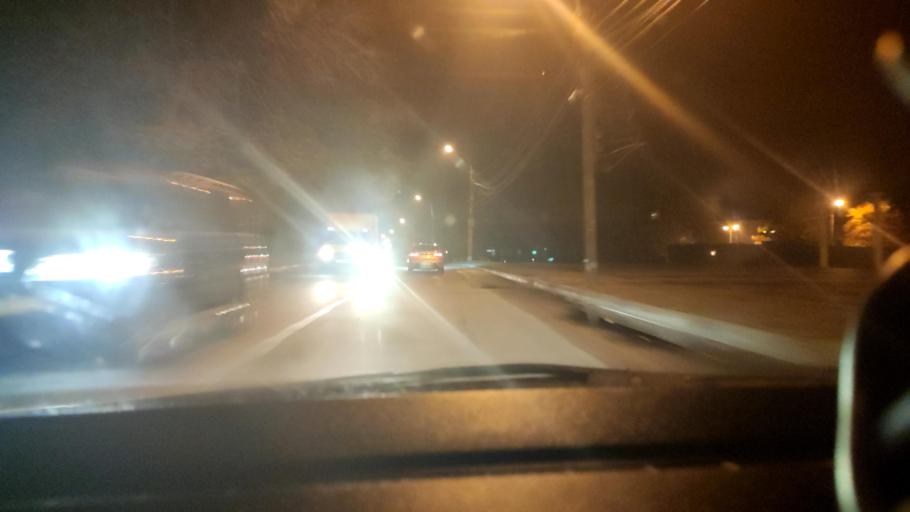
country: RU
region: Voronezj
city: Voronezh
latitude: 51.6582
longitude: 39.2146
